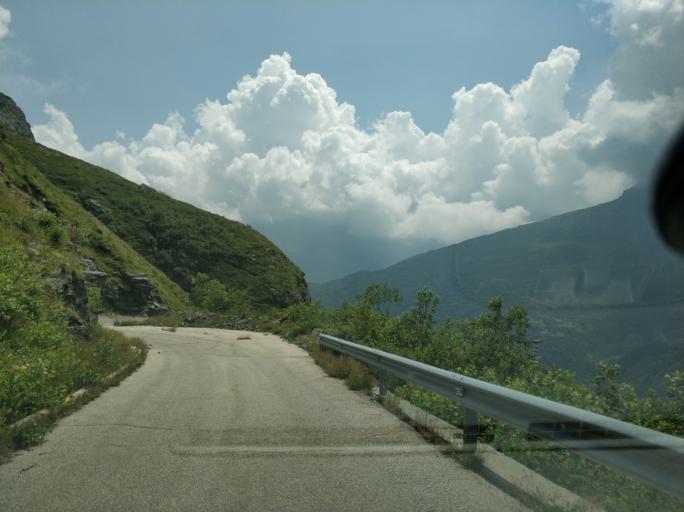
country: IT
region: Piedmont
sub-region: Provincia di Torino
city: Usseglio
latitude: 45.2529
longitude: 7.1800
